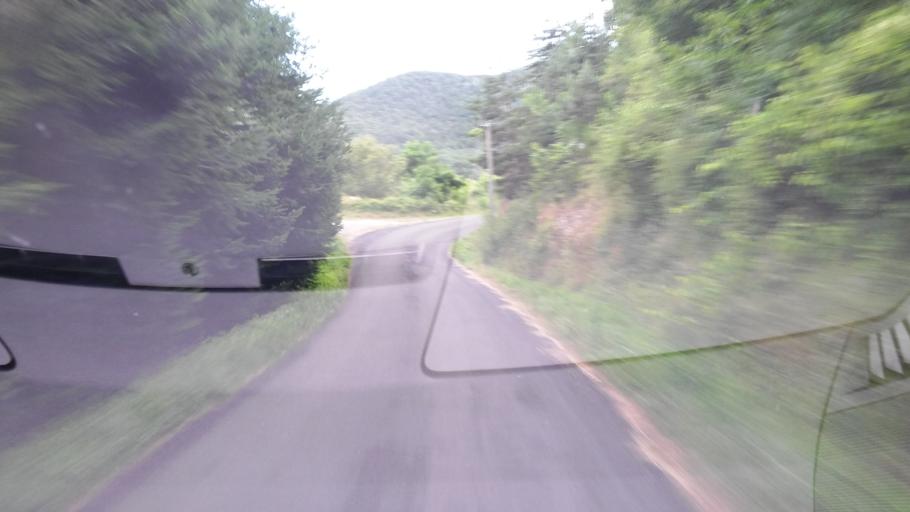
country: FR
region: Languedoc-Roussillon
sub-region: Departement de la Lozere
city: Meyrueis
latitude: 44.0218
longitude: 3.3436
